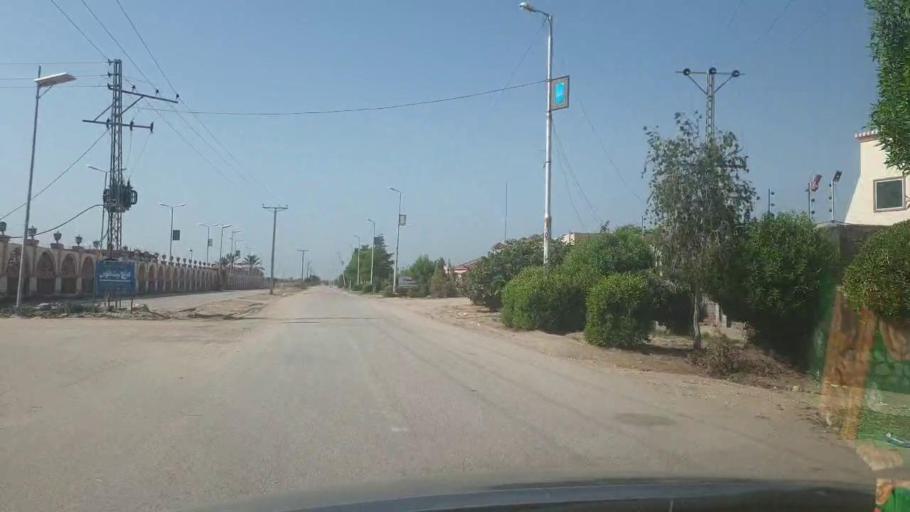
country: PK
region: Sindh
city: Rohri
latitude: 27.5226
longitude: 69.0365
